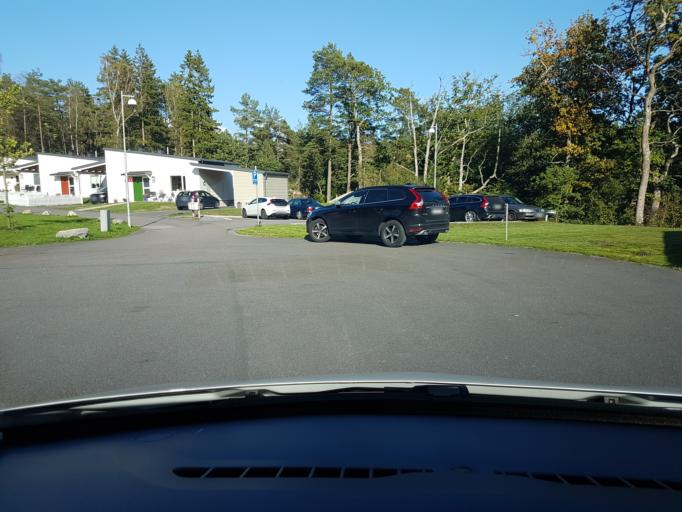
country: SE
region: Vaestra Goetaland
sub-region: Ale Kommun
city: Alafors
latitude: 57.9299
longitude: 12.0978
